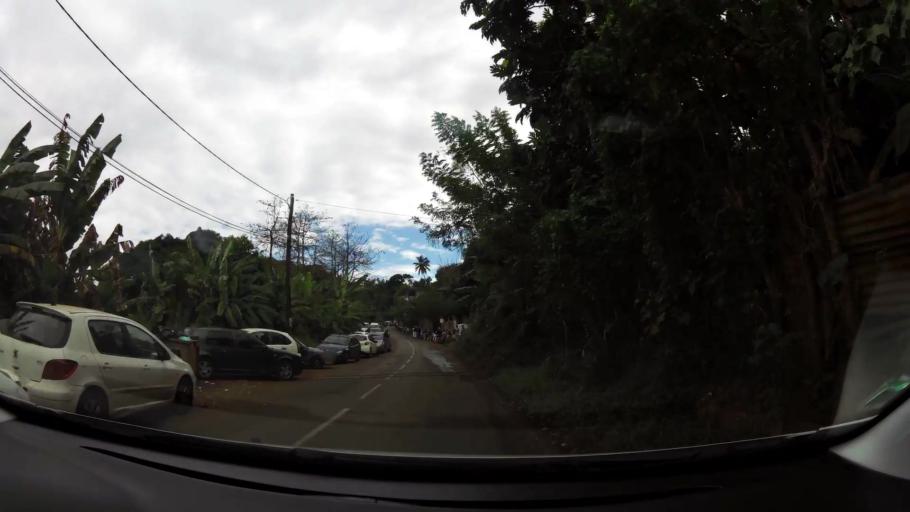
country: YT
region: Chiconi
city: Chiconi
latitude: -12.8358
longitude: 45.1148
